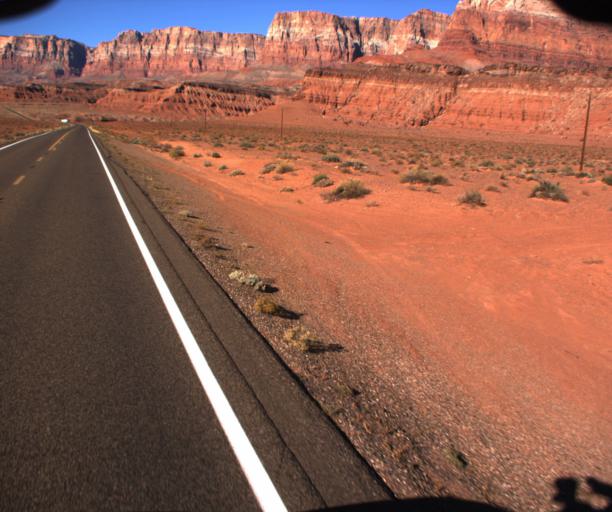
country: US
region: Arizona
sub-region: Coconino County
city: Page
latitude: 36.8139
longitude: -111.6492
